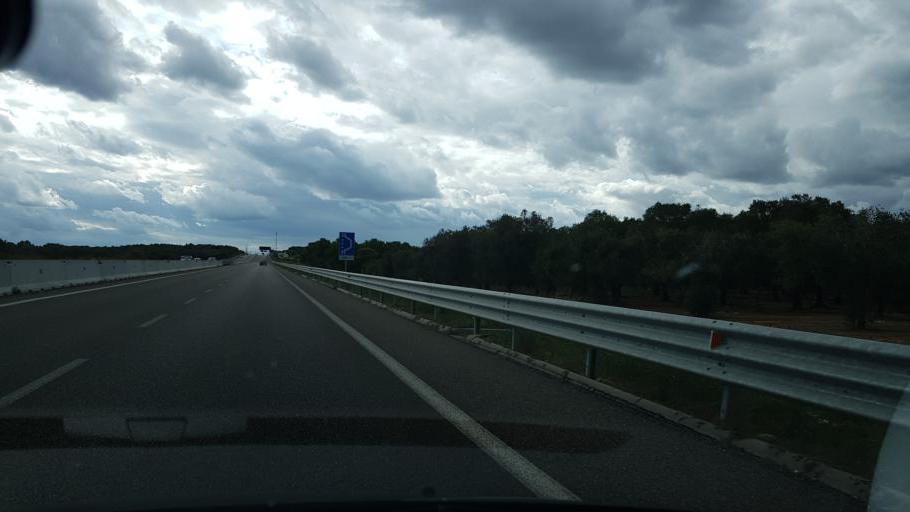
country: IT
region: Apulia
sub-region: Provincia di Lecce
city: Giurdignano
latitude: 40.1362
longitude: 18.4093
